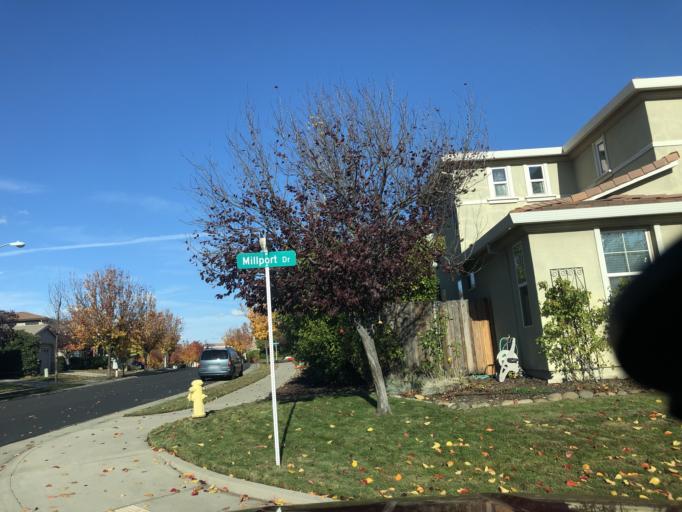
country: US
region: California
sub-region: Placer County
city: Roseville
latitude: 38.7911
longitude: -121.2864
